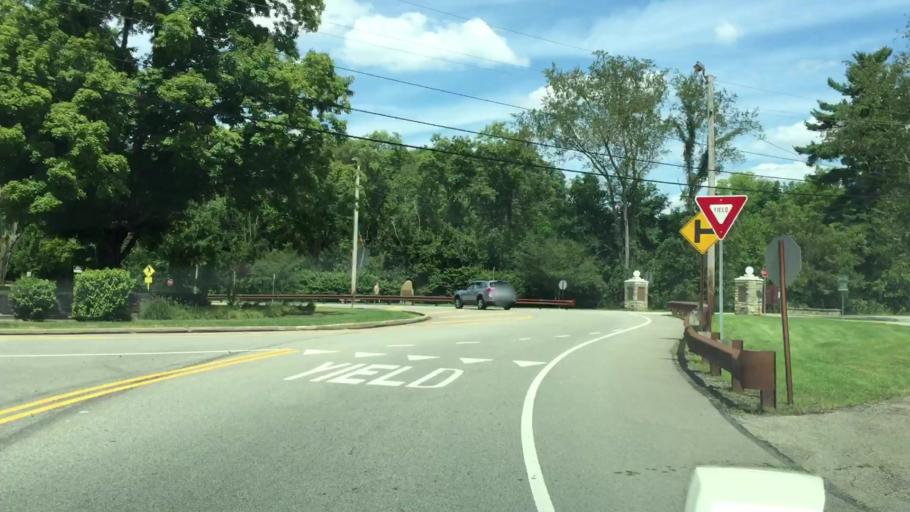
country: US
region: Pennsylvania
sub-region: Allegheny County
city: South Park Township
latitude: 40.3192
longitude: -80.0080
